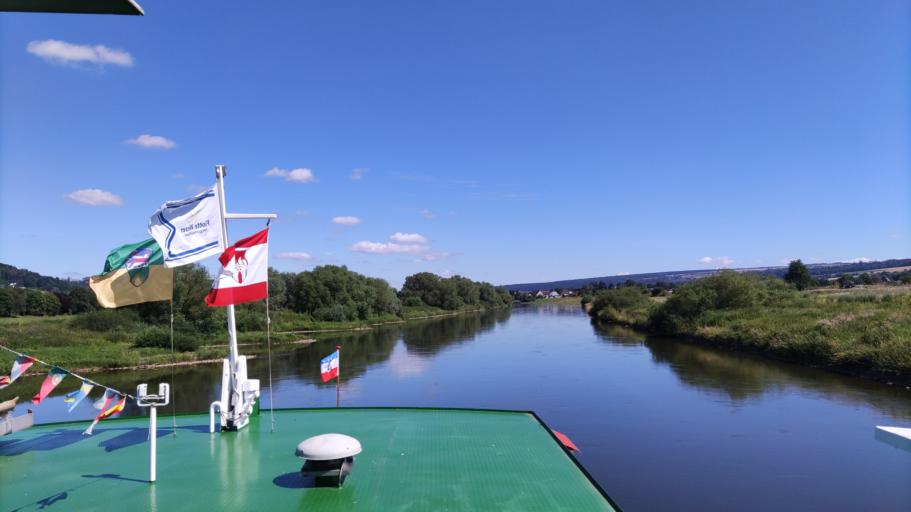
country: DE
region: North Rhine-Westphalia
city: Beverungen
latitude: 51.6510
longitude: 9.3751
